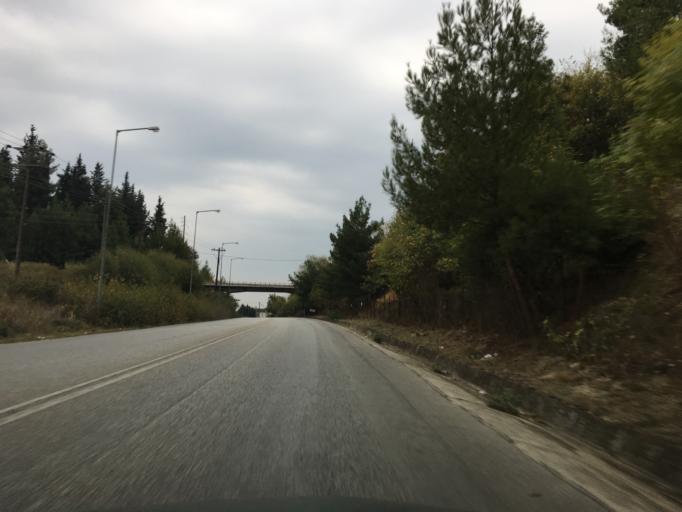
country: GR
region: Thessaly
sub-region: Trikala
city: Trikala
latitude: 39.5687
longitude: 21.7651
